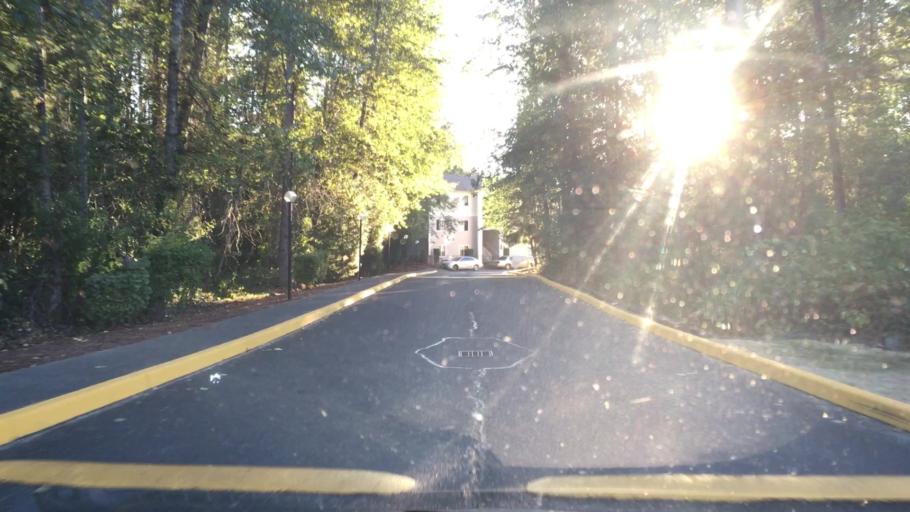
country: US
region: Washington
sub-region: King County
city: Lea Hill
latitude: 47.3257
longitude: -122.1775
